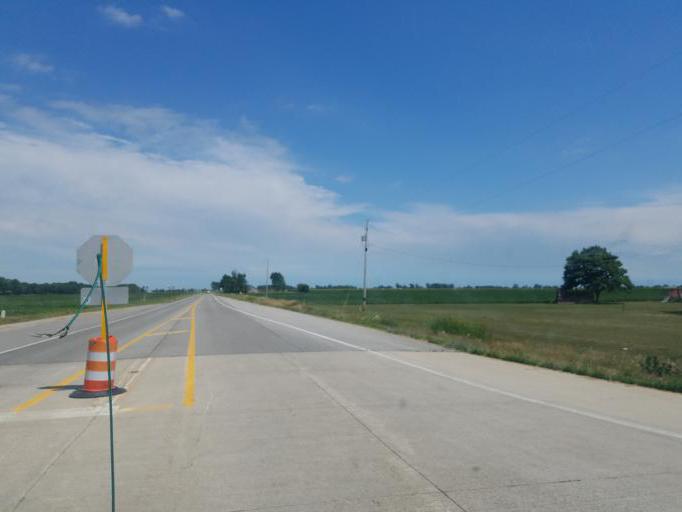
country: US
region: Indiana
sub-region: Allen County
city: Woodburn
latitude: 41.1542
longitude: -84.8485
